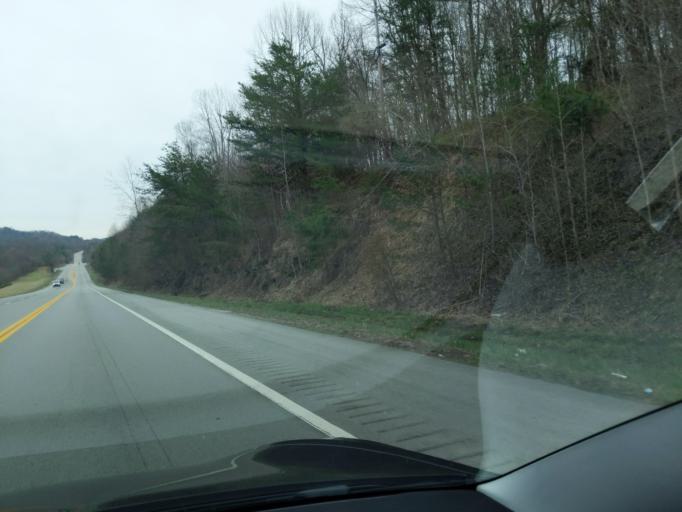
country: US
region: Kentucky
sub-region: Whitley County
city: Corbin
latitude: 36.9172
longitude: -84.0963
